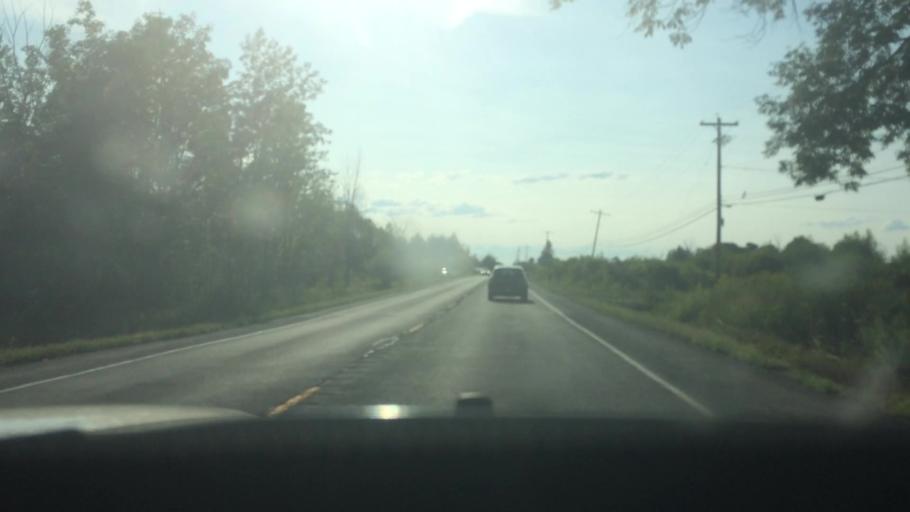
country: US
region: New York
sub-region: St. Lawrence County
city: Potsdam
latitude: 44.6700
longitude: -74.9469
